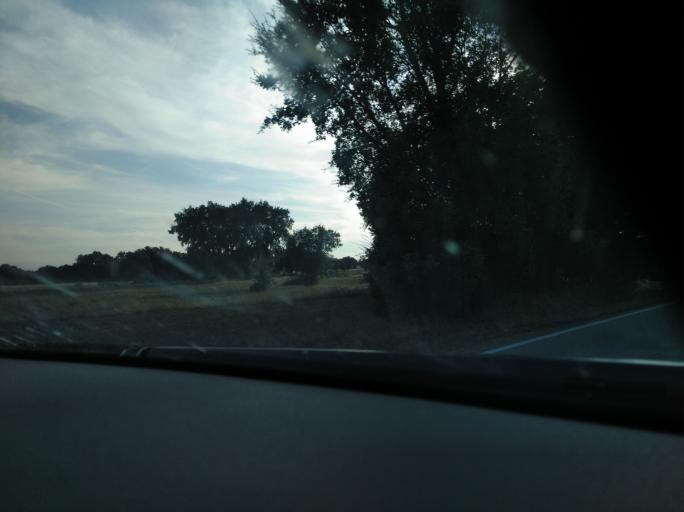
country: PT
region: Portalegre
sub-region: Fronteira
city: Fronteira
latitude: 38.9618
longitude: -7.5948
